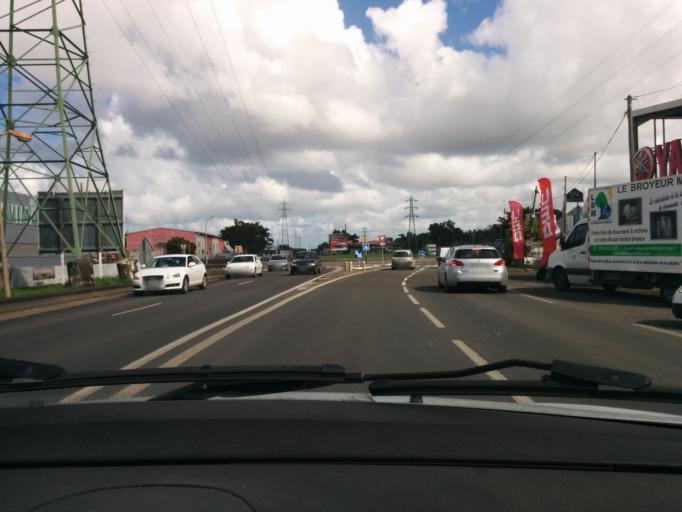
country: GP
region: Guadeloupe
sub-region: Guadeloupe
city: Pointe-a-Pitre
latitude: 16.2447
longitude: -61.5550
